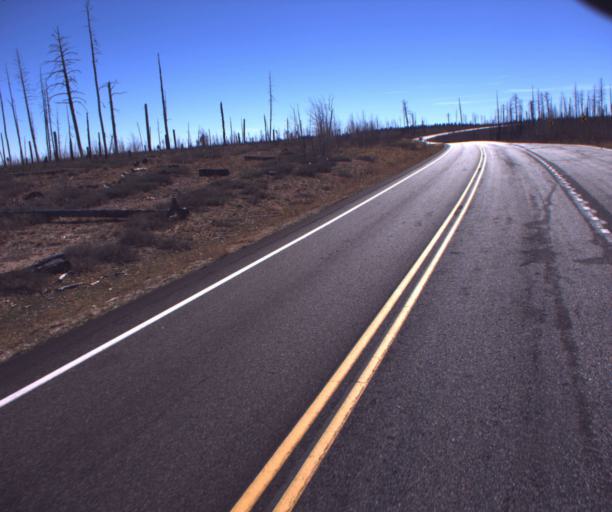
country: US
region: Arizona
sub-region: Coconino County
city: Grand Canyon
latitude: 36.5671
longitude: -112.1727
